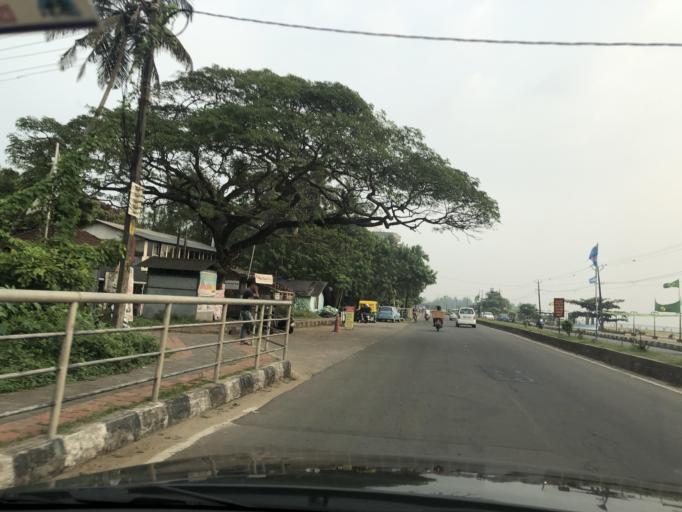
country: IN
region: Kerala
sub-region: Kozhikode
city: Kozhikode
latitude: 11.2795
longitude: 75.7626
